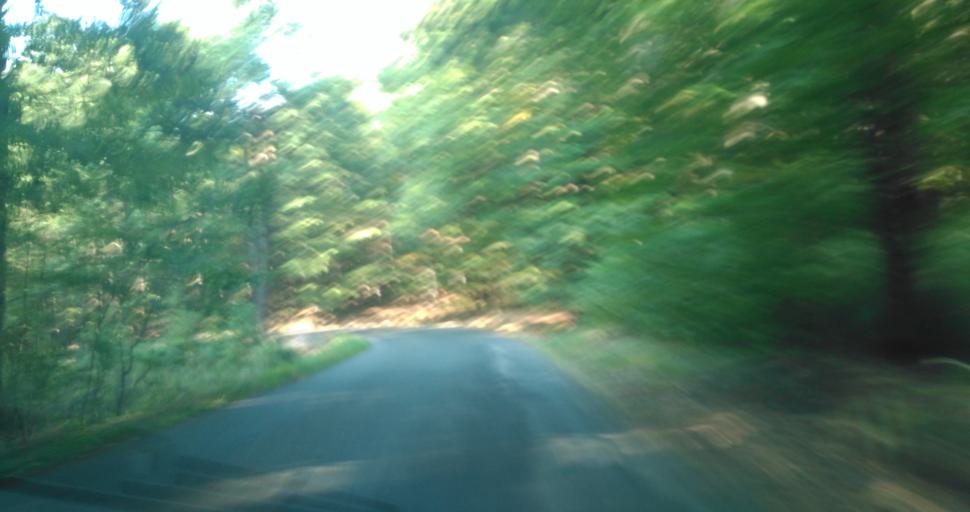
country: CZ
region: Central Bohemia
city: Roztoky
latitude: 49.9778
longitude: 13.8685
